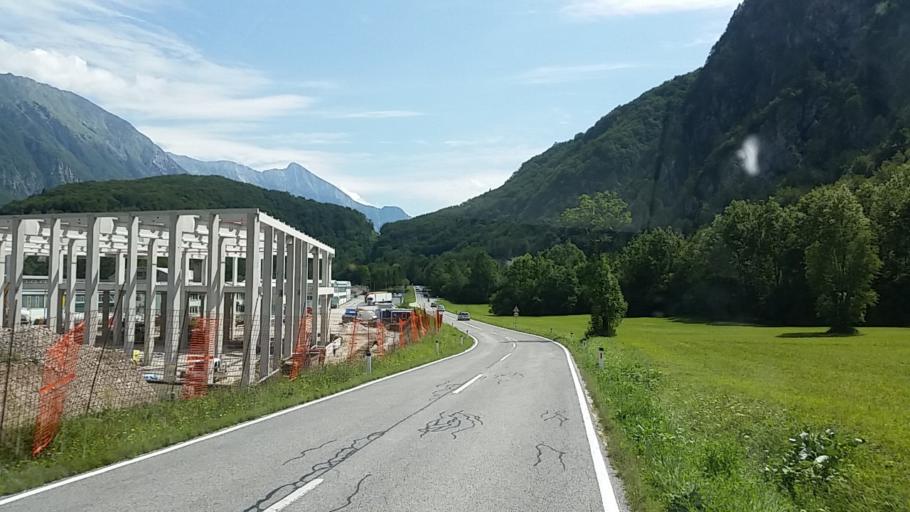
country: SI
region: Bovec
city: Bovec
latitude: 46.2844
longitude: 13.5137
